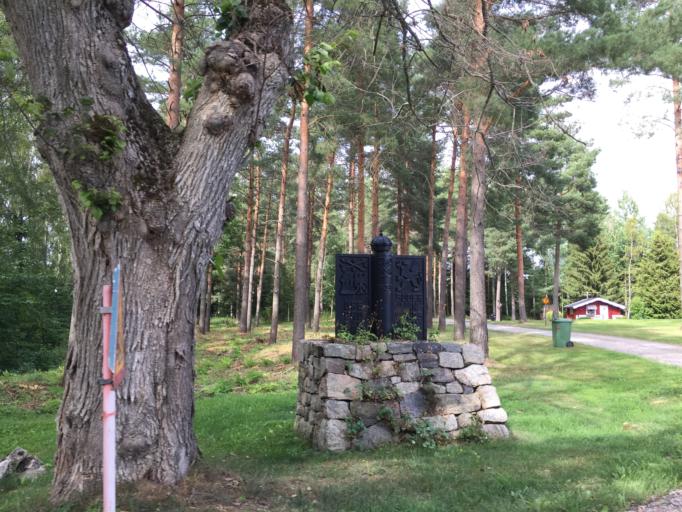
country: SE
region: Soedermanland
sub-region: Vingakers Kommun
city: Vingaker
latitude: 59.0944
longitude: 15.7011
